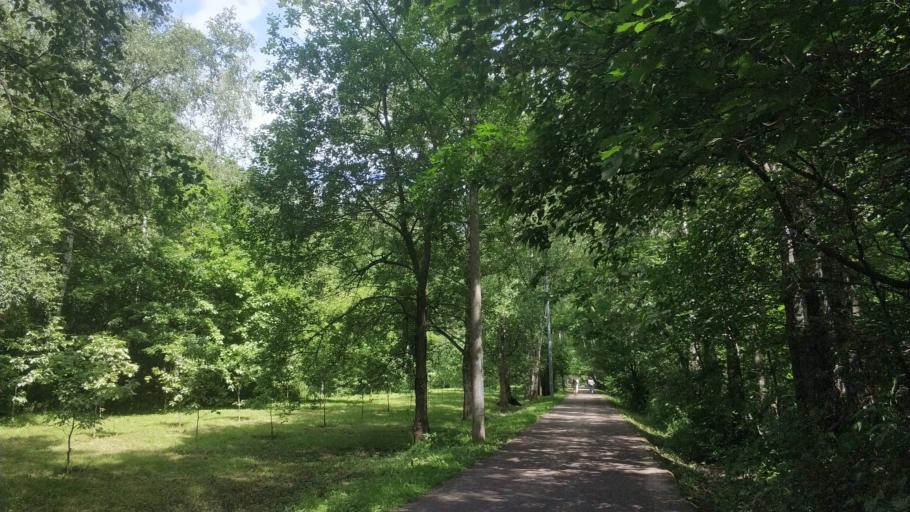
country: RU
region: Moscow
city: Perovo
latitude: 55.7287
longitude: 37.8013
